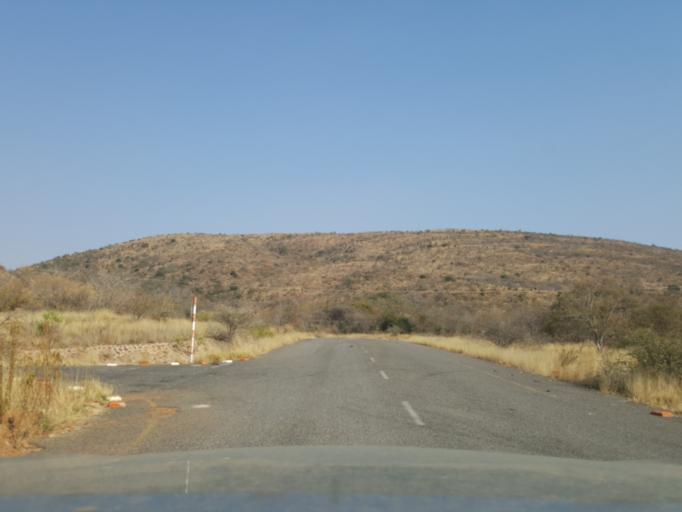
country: BW
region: South East
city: Lobatse
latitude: -25.1793
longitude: 25.6803
